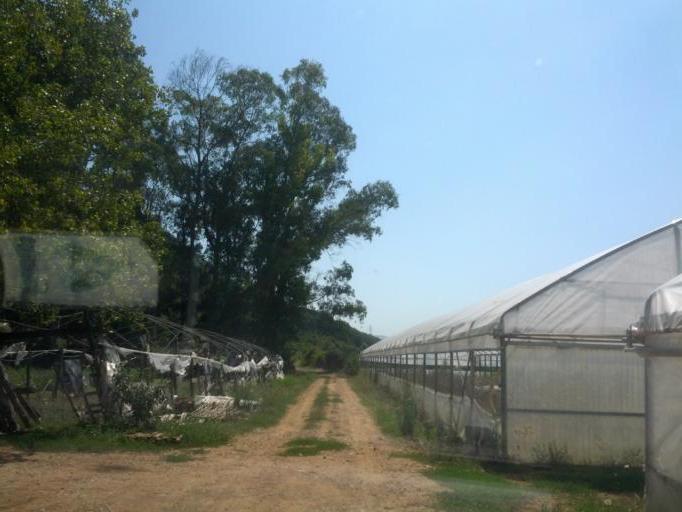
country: IT
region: Latium
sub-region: Provincia di Latina
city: Monte San Biagio
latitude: 41.3665
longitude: 13.3546
